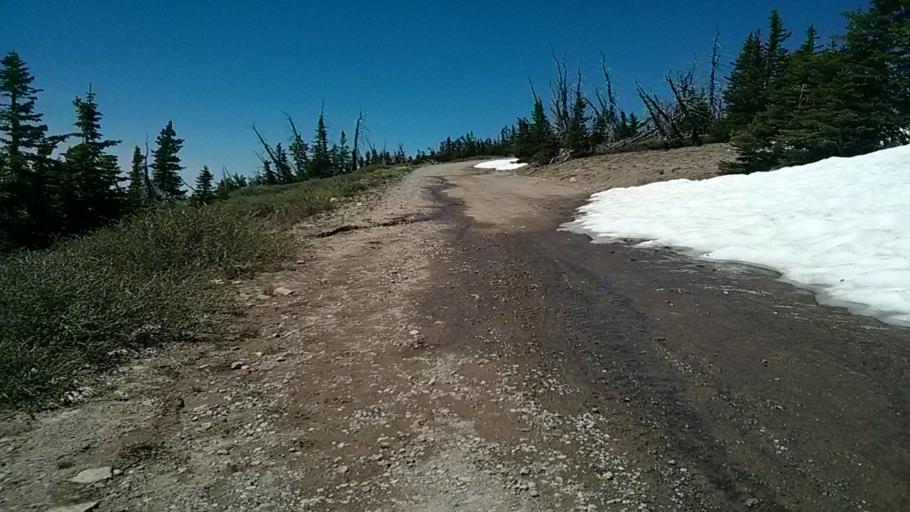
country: US
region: Utah
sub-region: Iron County
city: Parowan
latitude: 37.6841
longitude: -112.8229
